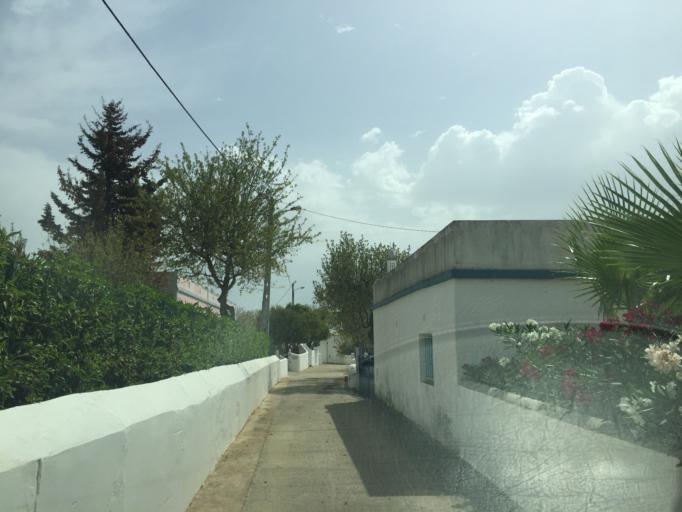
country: PT
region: Faro
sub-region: Loule
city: Boliqueime
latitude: 37.1299
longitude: -8.1366
